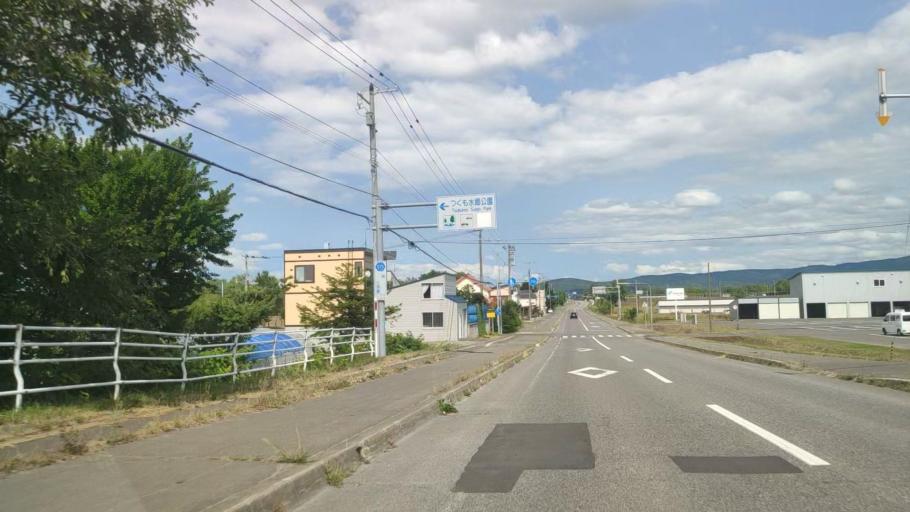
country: JP
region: Hokkaido
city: Nayoro
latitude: 44.1875
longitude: 142.4077
